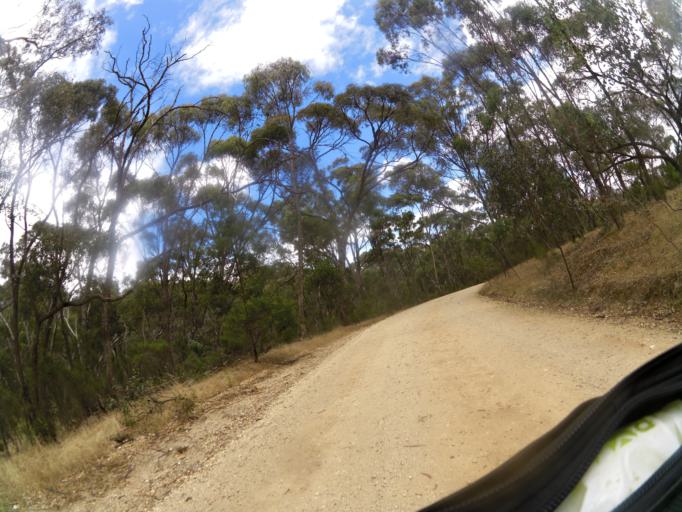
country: AU
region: Victoria
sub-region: Mount Alexander
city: Castlemaine
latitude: -37.0317
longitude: 144.2600
